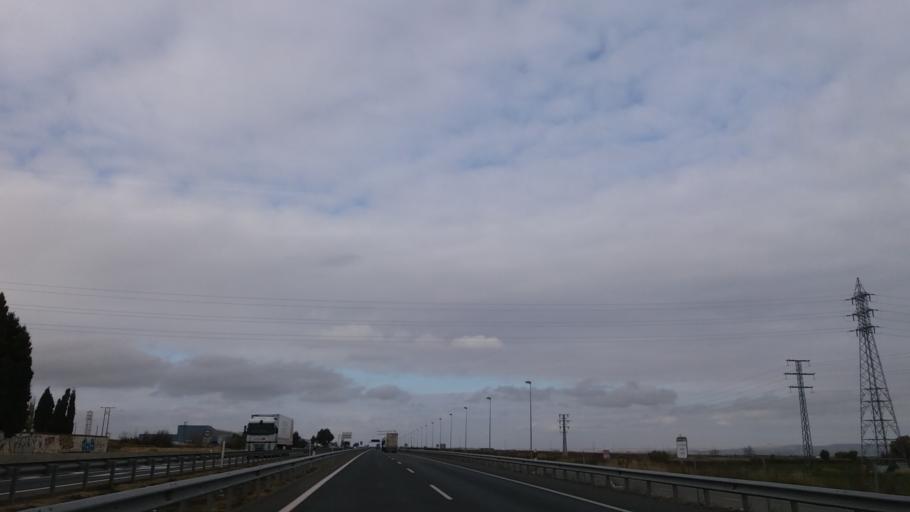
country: ES
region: Navarre
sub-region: Provincia de Navarra
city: Cortes
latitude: 41.9221
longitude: -1.4462
